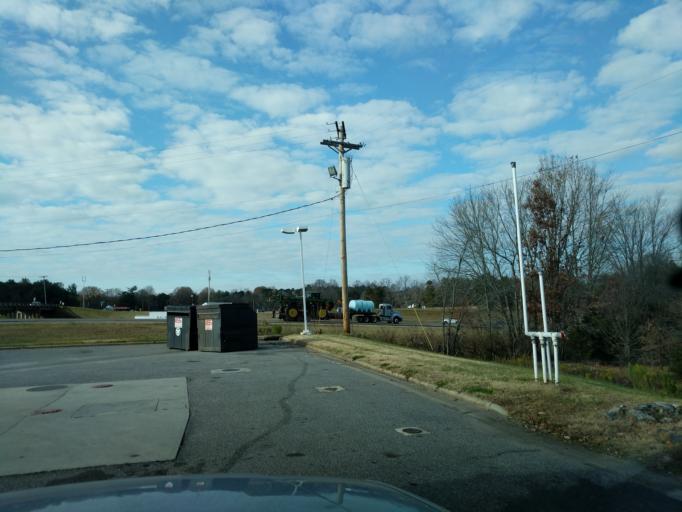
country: US
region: North Carolina
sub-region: Alexander County
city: Stony Point
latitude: 35.7719
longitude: -80.9958
